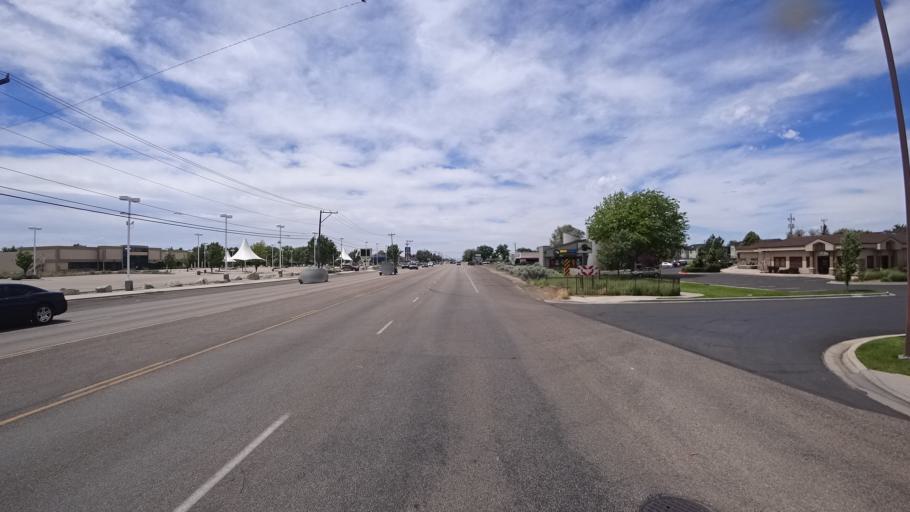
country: US
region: Idaho
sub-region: Ada County
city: Garden City
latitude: 43.6195
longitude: -116.3069
